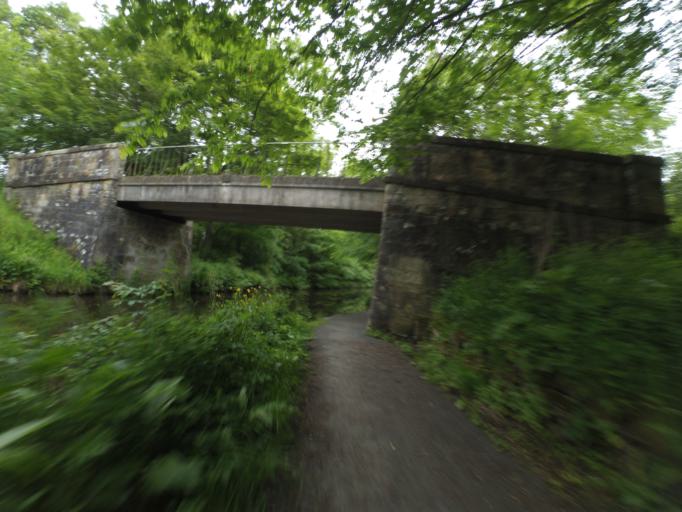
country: GB
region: Scotland
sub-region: West Lothian
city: Broxburn
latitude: 55.9692
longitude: -3.4730
